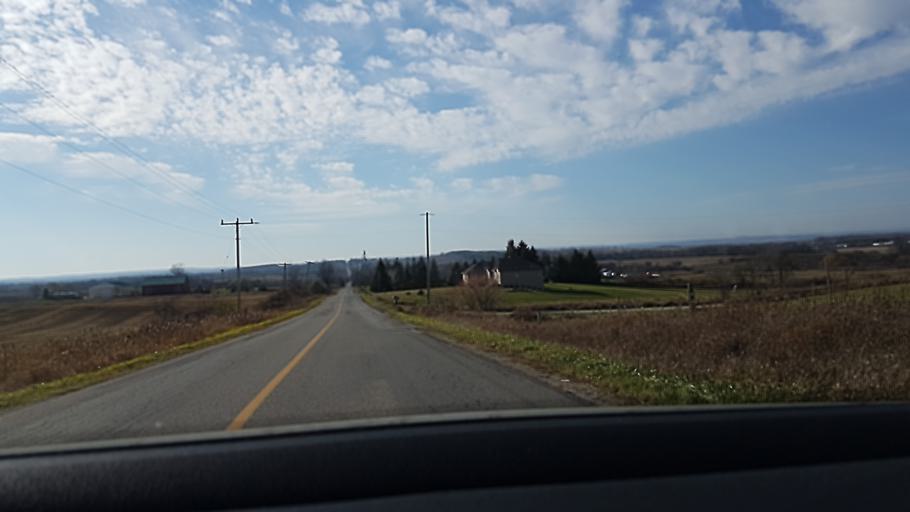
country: CA
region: Ontario
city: Bradford West Gwillimbury
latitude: 44.0643
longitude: -79.7905
